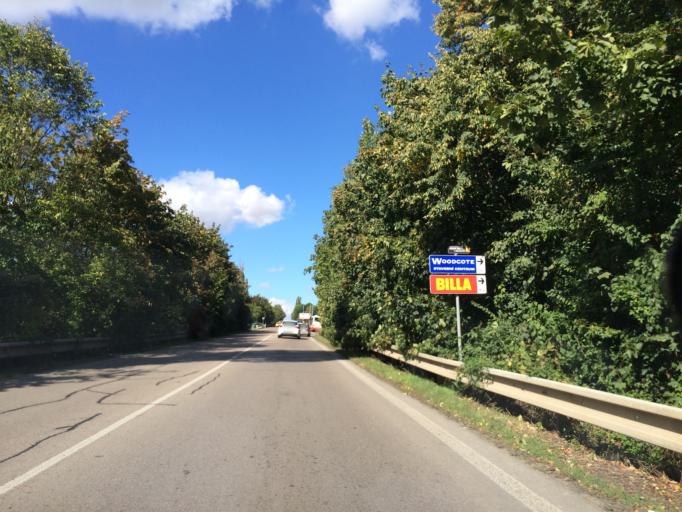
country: CZ
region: Central Bohemia
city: Hostivice
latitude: 50.0861
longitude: 14.3071
